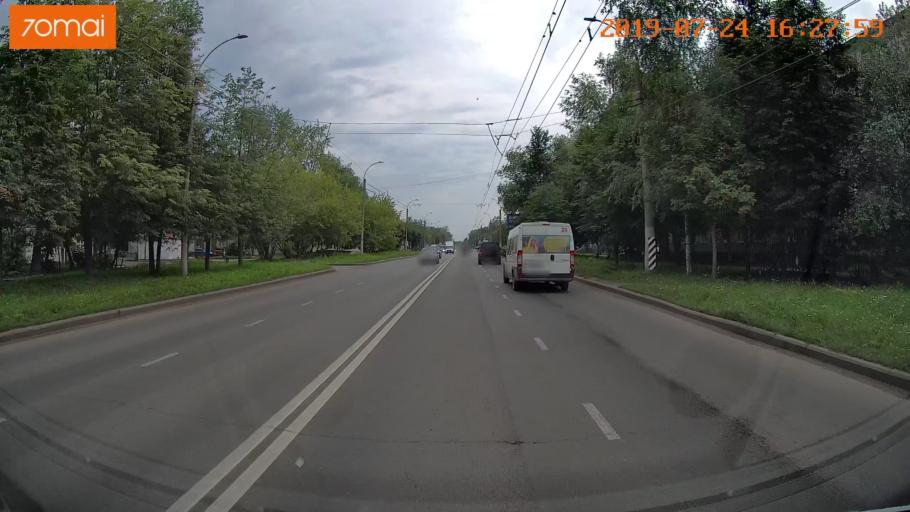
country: RU
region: Ivanovo
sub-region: Gorod Ivanovo
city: Ivanovo
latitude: 56.9747
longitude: 40.9652
